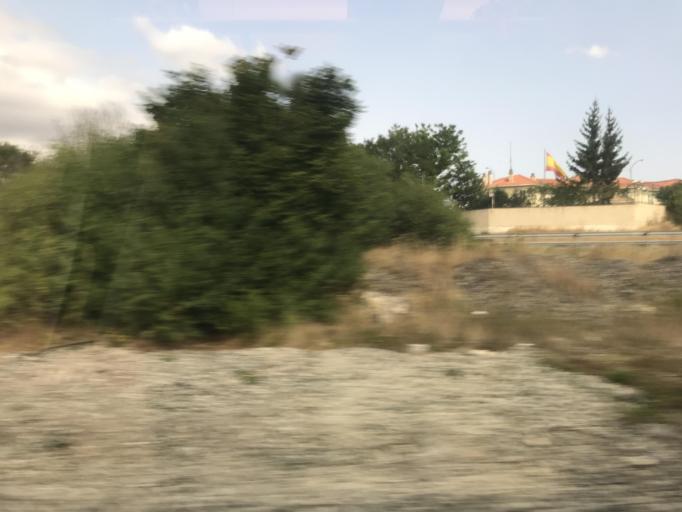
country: ES
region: Basque Country
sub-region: Provincia de Alava
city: Arminon
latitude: 42.7692
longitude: -2.8303
